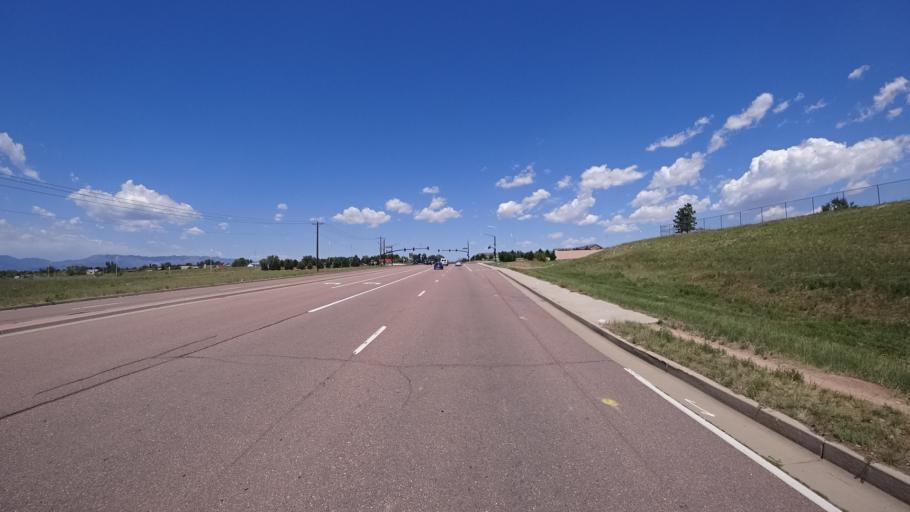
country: US
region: Colorado
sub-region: El Paso County
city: Security-Widefield
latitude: 38.7792
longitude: -104.7388
